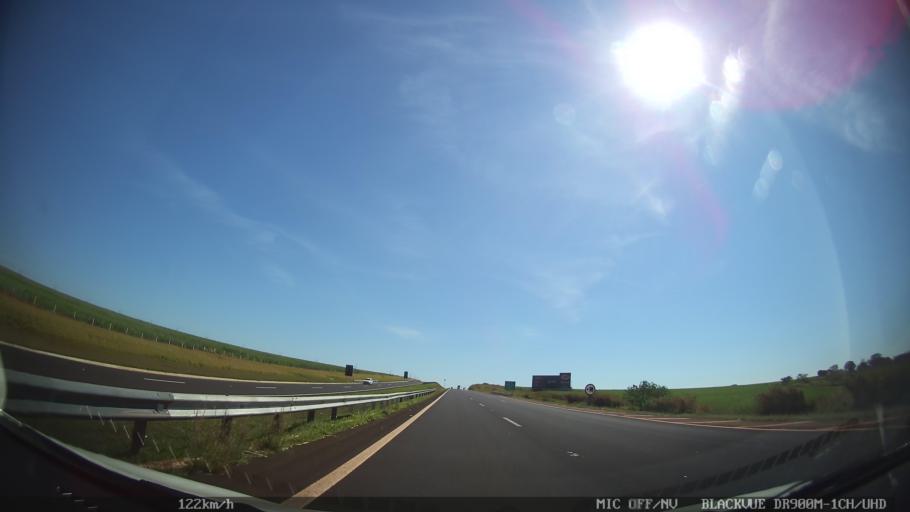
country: BR
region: Sao Paulo
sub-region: Cravinhos
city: Cravinhos
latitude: -21.3755
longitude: -47.7092
